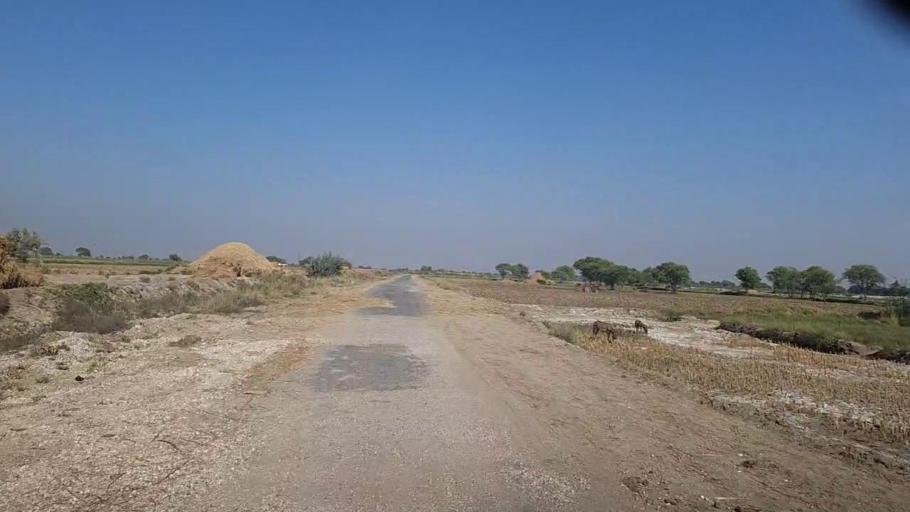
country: PK
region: Sindh
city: Tangwani
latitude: 28.2659
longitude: 68.9355
